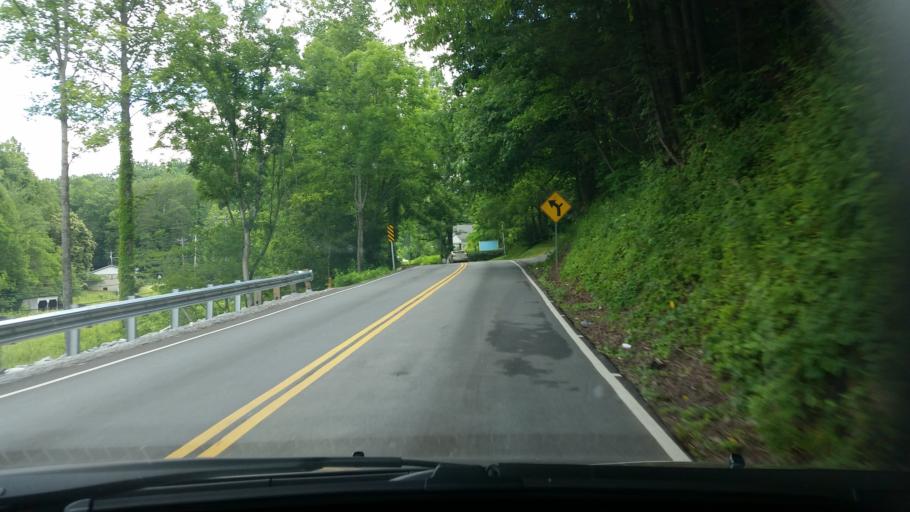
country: US
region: Tennessee
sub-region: Sevier County
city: Gatlinburg
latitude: 35.7289
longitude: -83.4684
